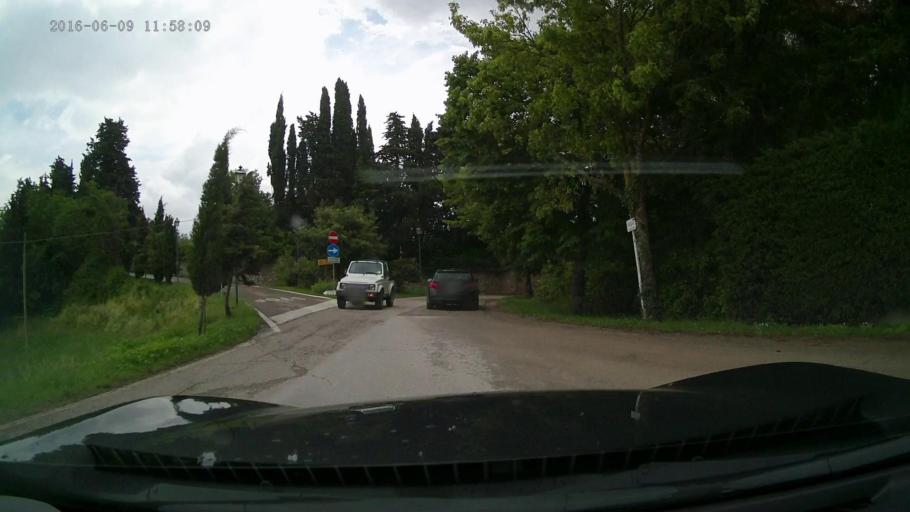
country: IT
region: Tuscany
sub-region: Province of Florence
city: Panzano in Chianti
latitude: 43.5486
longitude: 11.3063
